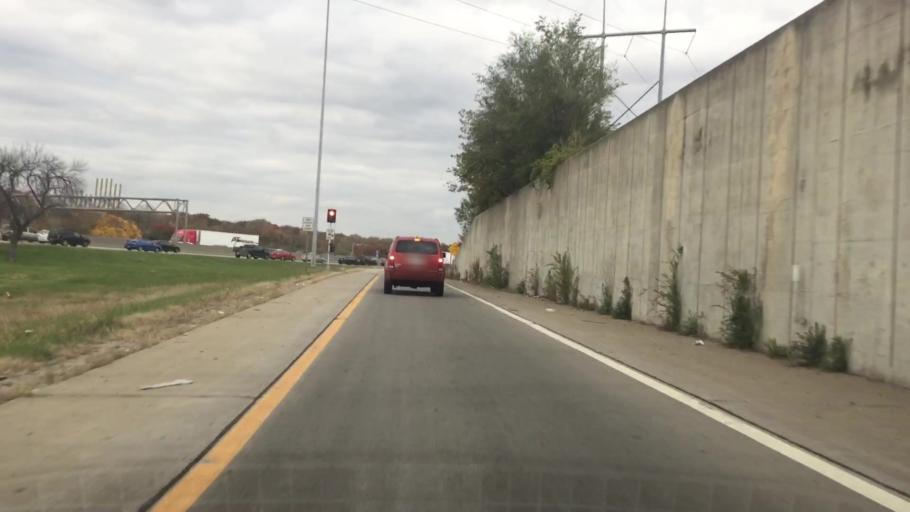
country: US
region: Kansas
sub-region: Johnson County
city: Merriam
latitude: 39.0234
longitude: -94.6904
